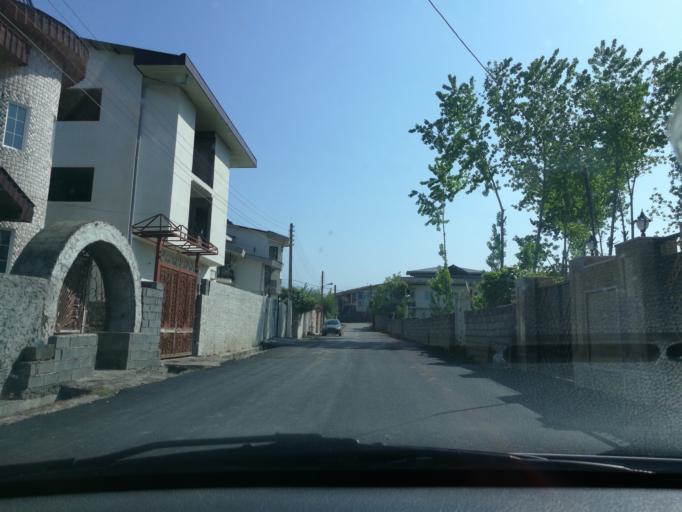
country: IR
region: Mazandaran
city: Chalus
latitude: 36.6703
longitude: 51.4323
